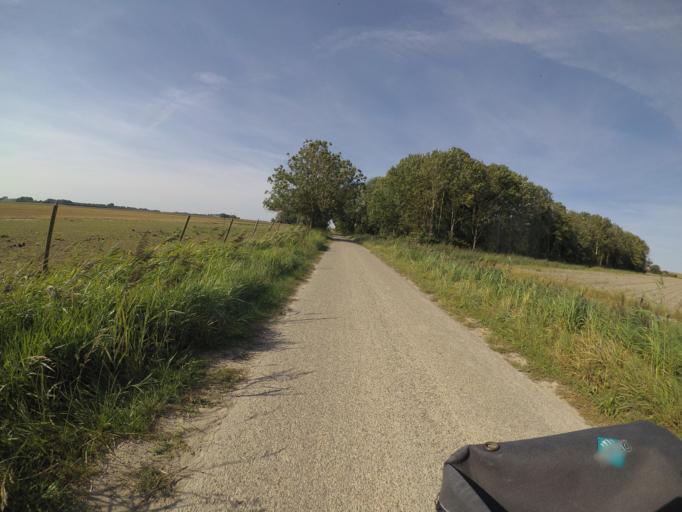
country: NL
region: Friesland
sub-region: Gemeente Ferwerderadiel
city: Ferwert
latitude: 53.3424
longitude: 5.8086
